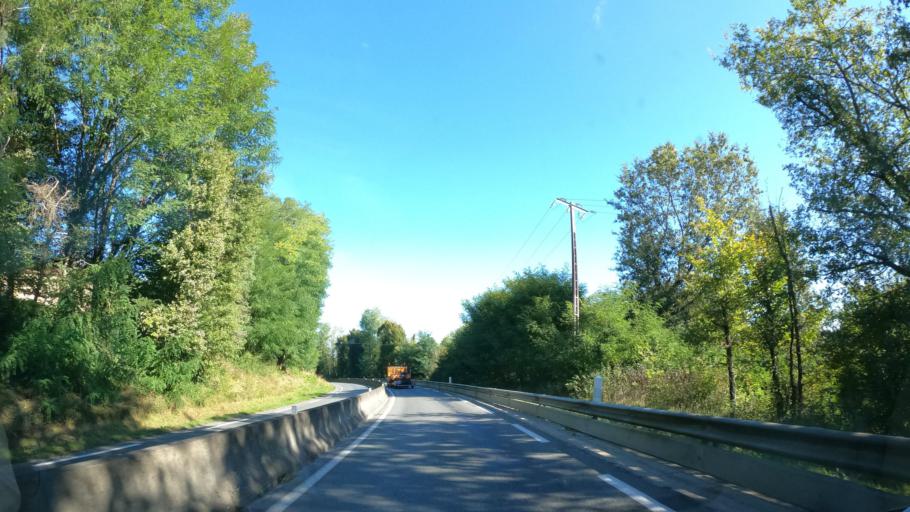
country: FR
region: Aquitaine
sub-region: Departement de la Dordogne
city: Notre-Dame-de-Sanilhac
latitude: 45.1274
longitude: 0.7010
